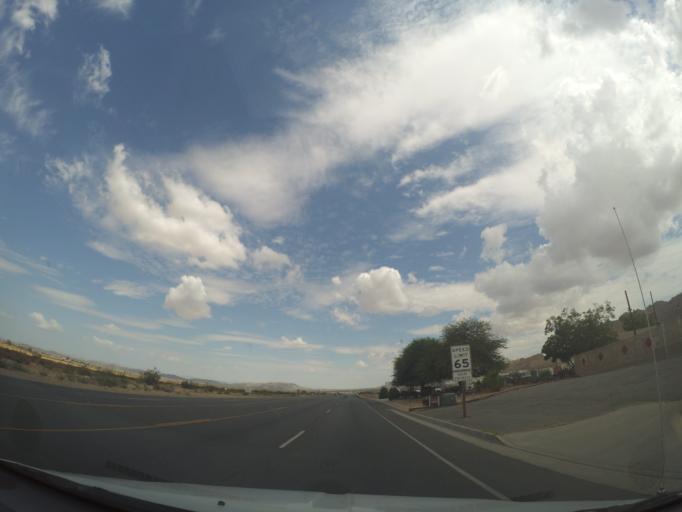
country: US
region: California
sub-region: San Bernardino County
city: Joshua Tree
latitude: 34.1349
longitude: -116.3018
